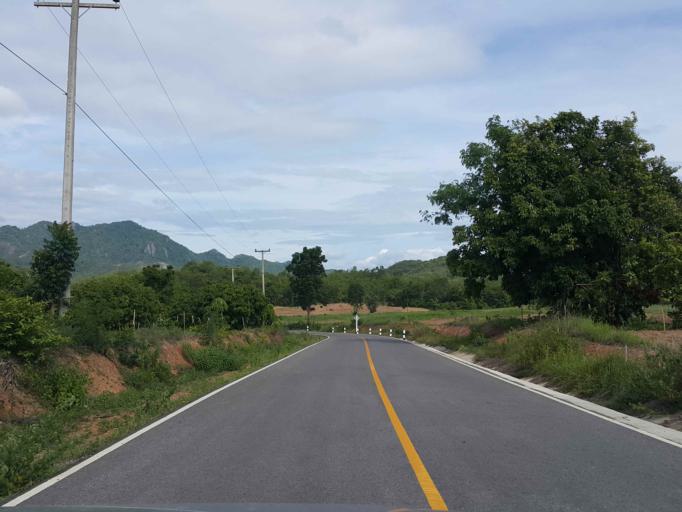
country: TH
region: Sukhothai
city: Thung Saliam
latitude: 17.2370
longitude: 99.5061
